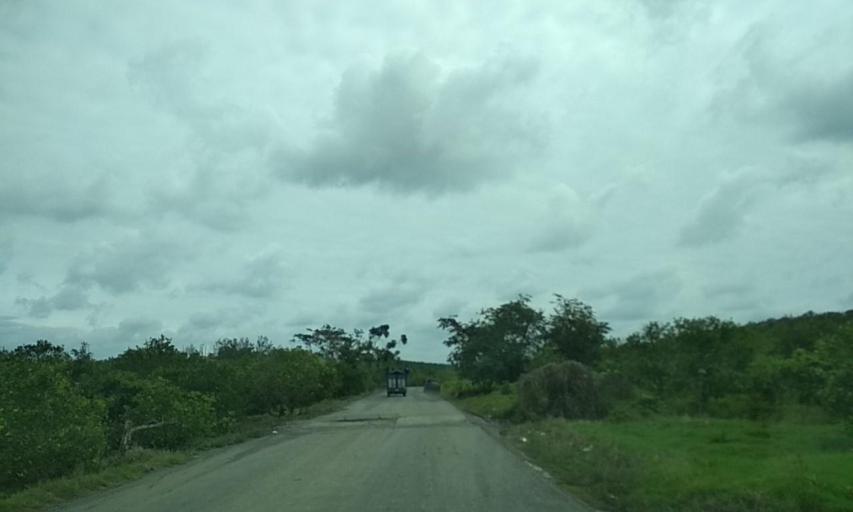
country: MX
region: Veracruz
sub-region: Papantla
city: El Chote
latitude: 20.3526
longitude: -97.3566
